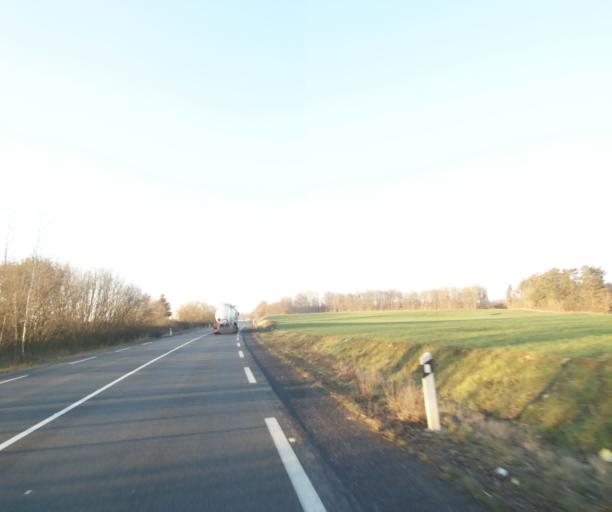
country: FR
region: Champagne-Ardenne
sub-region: Departement de la Haute-Marne
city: Bienville
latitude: 48.5475
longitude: 5.0672
